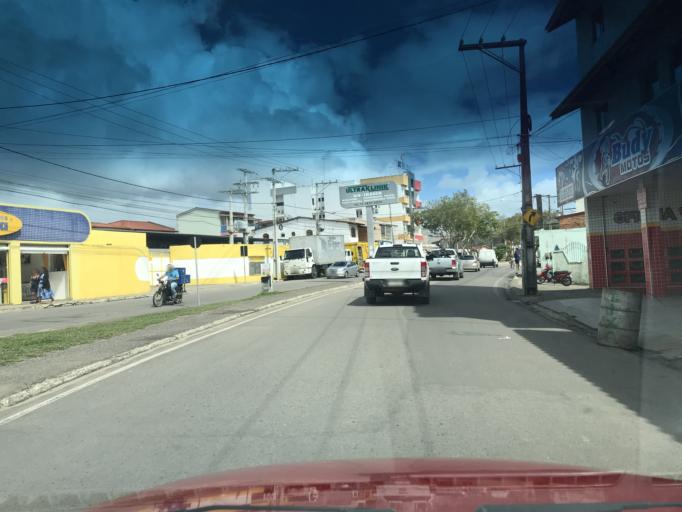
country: BR
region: Bahia
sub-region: Santo Antonio De Jesus
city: Santo Antonio de Jesus
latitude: -12.9795
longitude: -39.2767
